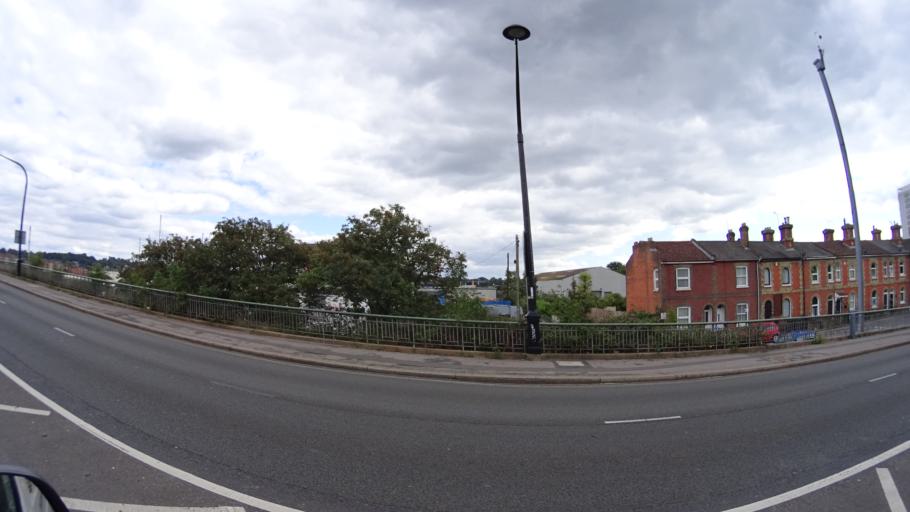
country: GB
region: England
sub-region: Southampton
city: Southampton
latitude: 50.9129
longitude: -1.3875
